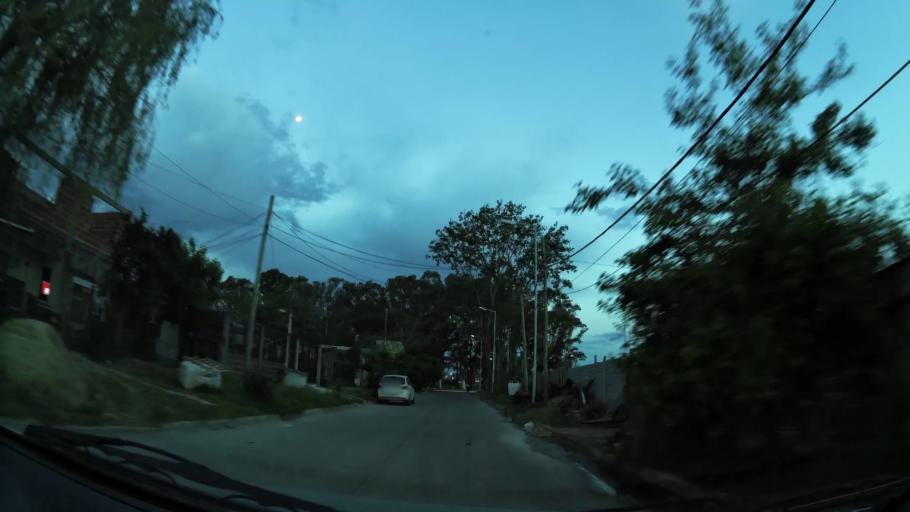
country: AR
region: Buenos Aires
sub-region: Partido de Avellaneda
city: Avellaneda
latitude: -34.6766
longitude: -58.3377
